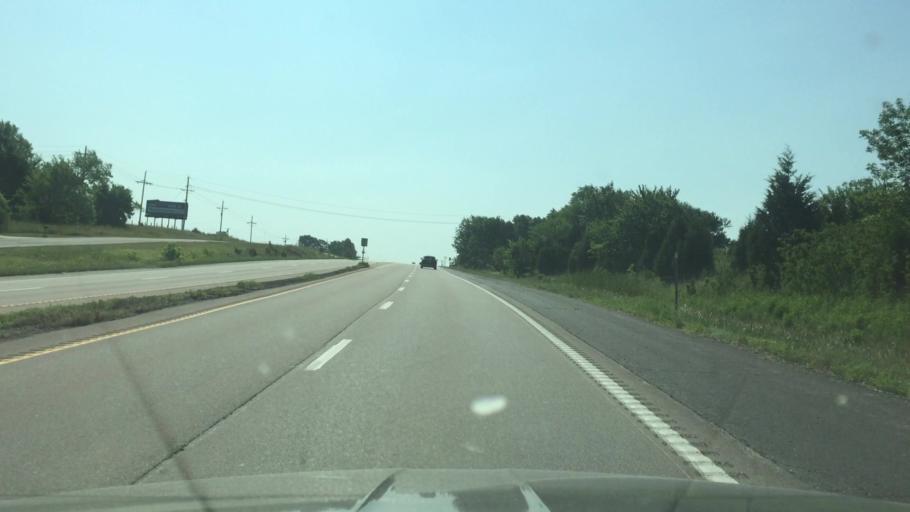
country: US
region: Missouri
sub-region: Pettis County
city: Sedalia
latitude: 38.7200
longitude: -93.2972
